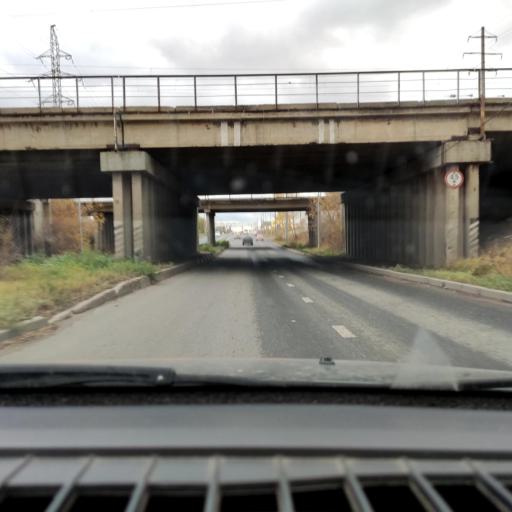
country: RU
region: Samara
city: Tol'yatti
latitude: 53.5672
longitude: 49.2910
